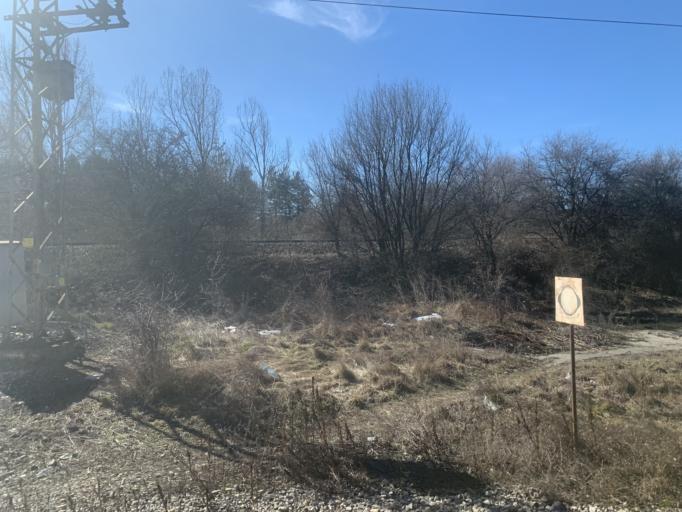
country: BG
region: Sofiya
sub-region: Obshtina Gorna Malina
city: Gorna Malina
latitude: 42.5585
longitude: 23.7016
